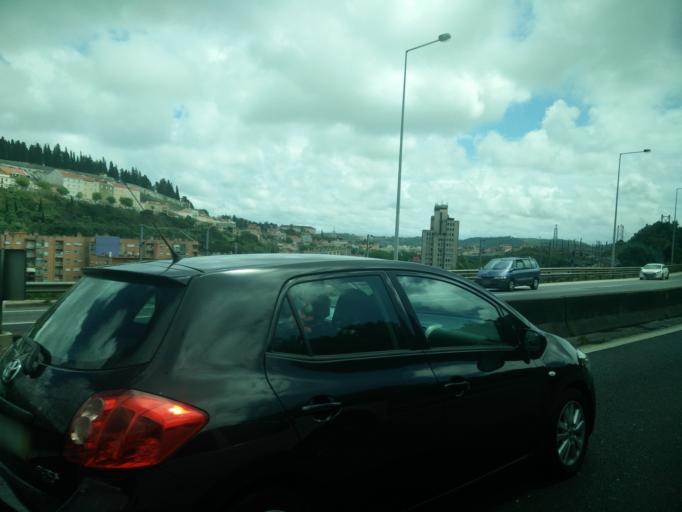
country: PT
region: Setubal
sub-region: Almada
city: Cacilhas
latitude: 38.7157
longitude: -9.1771
